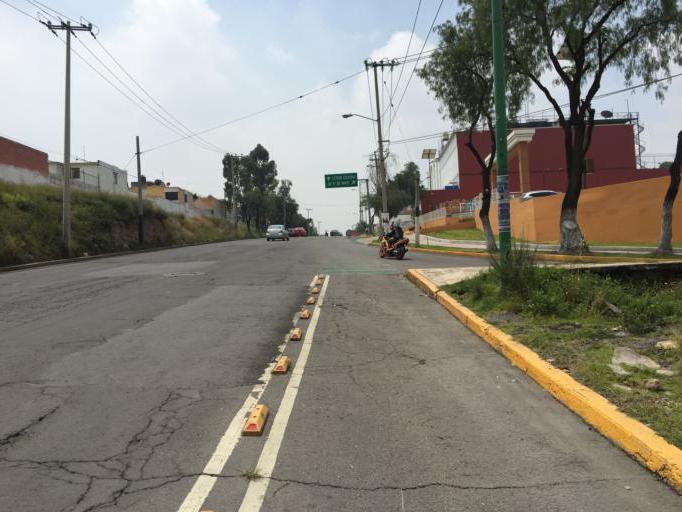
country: MX
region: Mexico
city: Cuautitlan Izcalli
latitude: 19.6428
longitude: -99.2039
